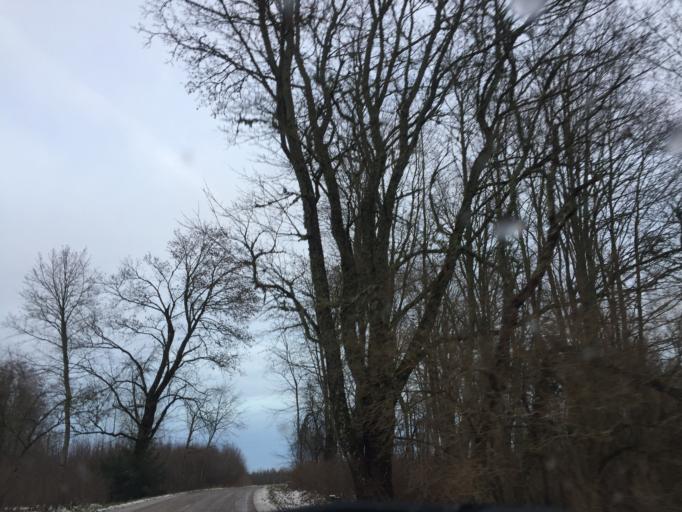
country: LV
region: Limbazu Rajons
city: Limbazi
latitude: 57.5646
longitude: 24.8190
